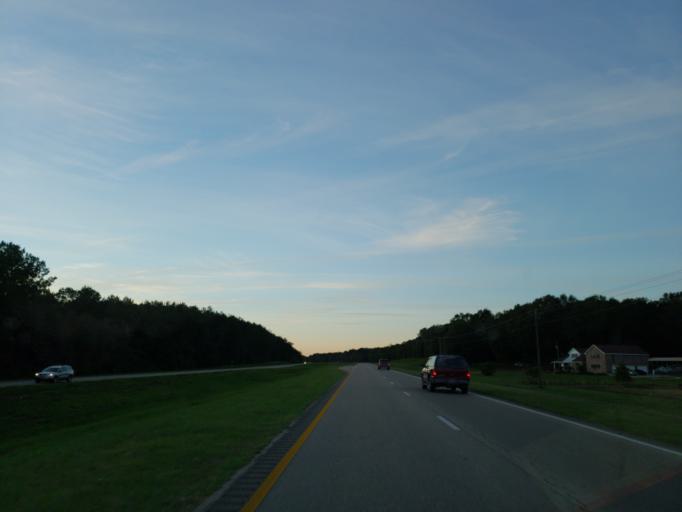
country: US
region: Mississippi
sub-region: Wayne County
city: Belmont
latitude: 31.5972
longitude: -88.5543
